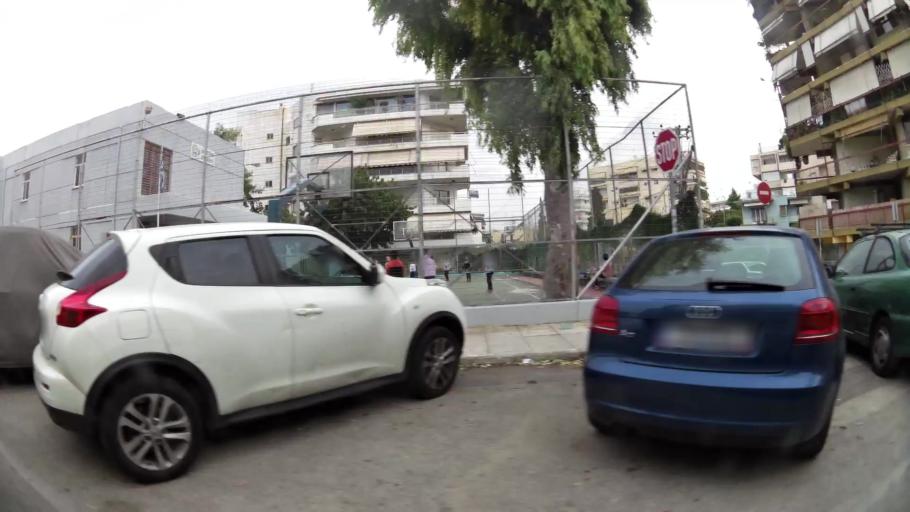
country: GR
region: Attica
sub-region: Nomarchia Athinas
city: Palaio Faliro
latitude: 37.9187
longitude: 23.7069
